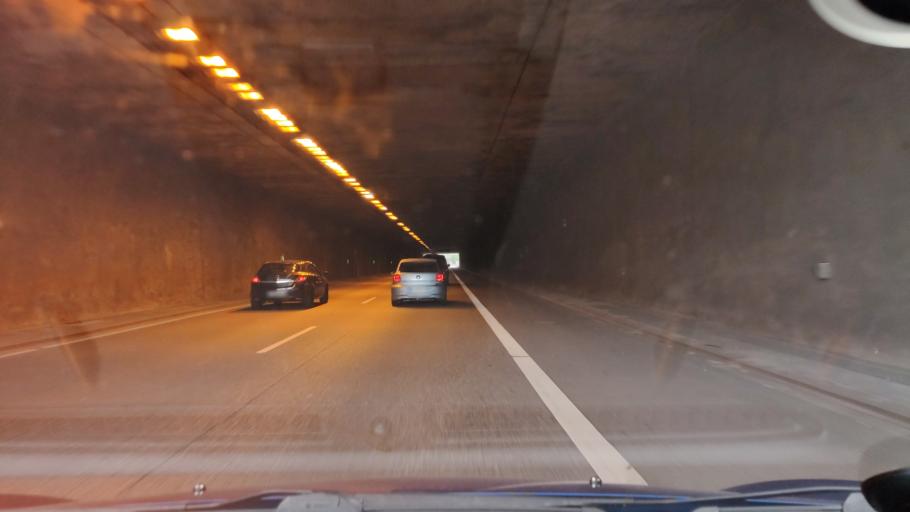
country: DE
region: Schleswig-Holstein
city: Kiel
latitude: 54.3562
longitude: 10.1194
